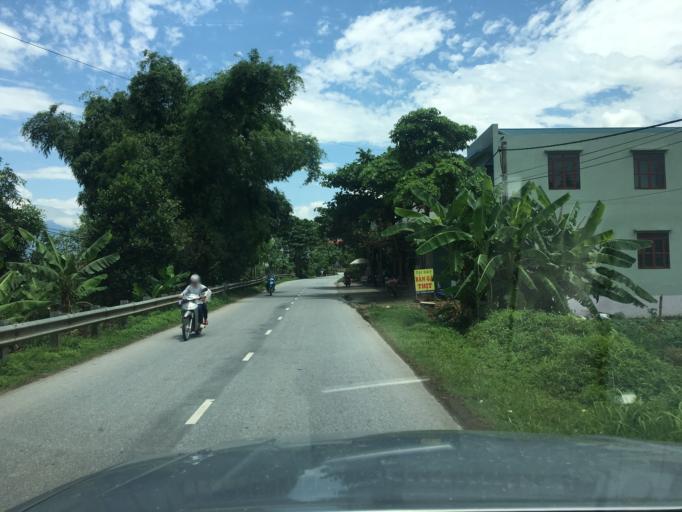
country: VN
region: Yen Bai
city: Son Thinh
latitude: 21.6456
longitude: 104.5009
